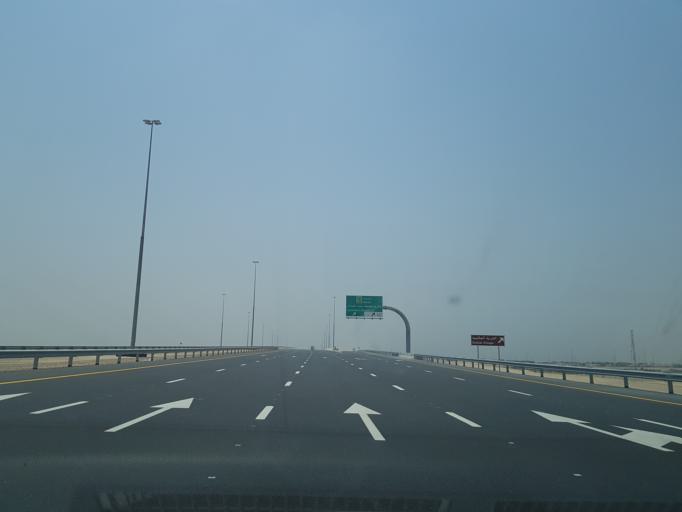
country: AE
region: Dubai
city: Dubai
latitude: 25.0620
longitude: 55.3071
